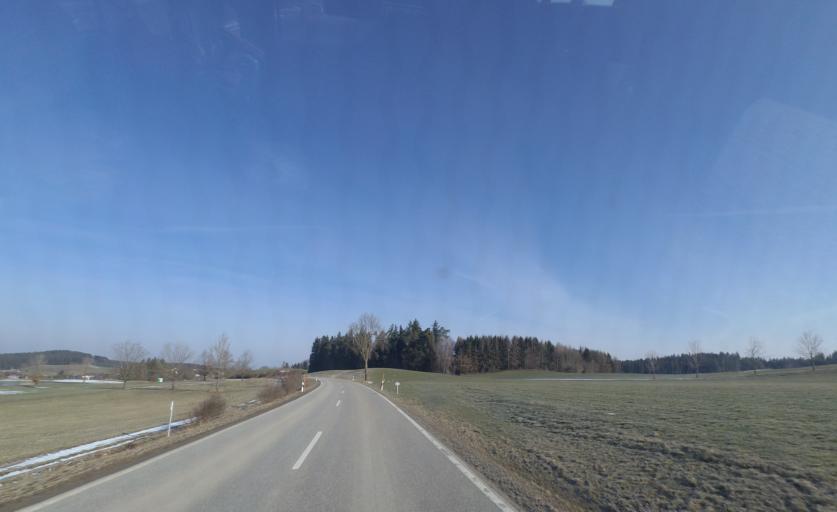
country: DE
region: Bavaria
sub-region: Upper Bavaria
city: Traunreut
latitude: 47.9397
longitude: 12.5533
